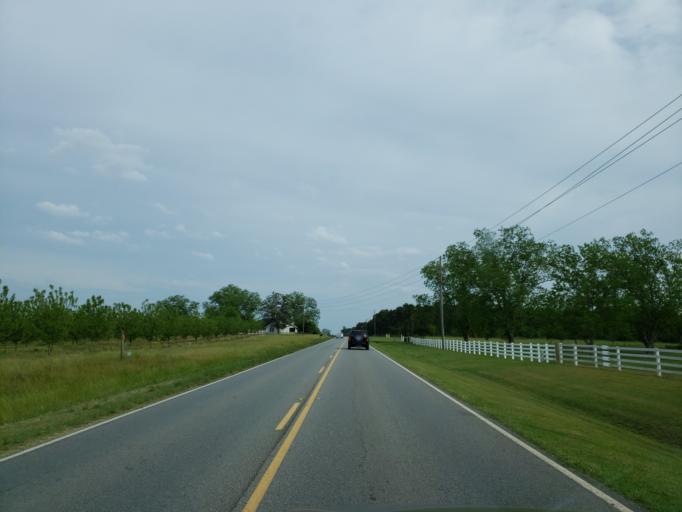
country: US
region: Georgia
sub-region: Dooly County
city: Vienna
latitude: 32.1087
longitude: -83.8275
